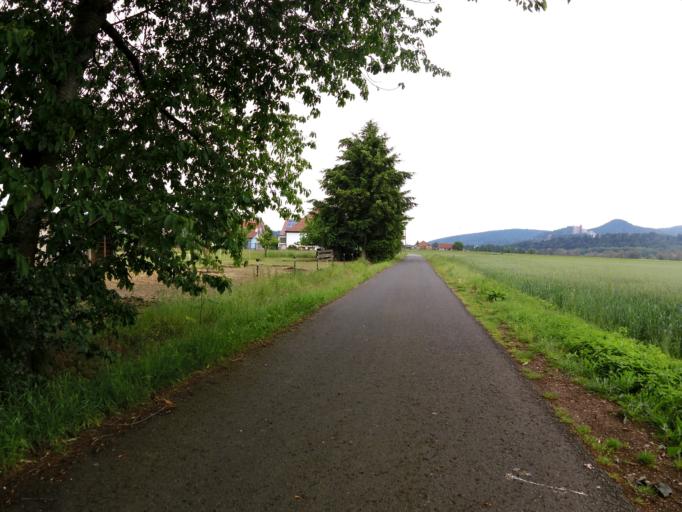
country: DE
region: Hesse
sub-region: Regierungsbezirk Kassel
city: Rotenburg an der Fulda
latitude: 50.9832
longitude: 9.7568
